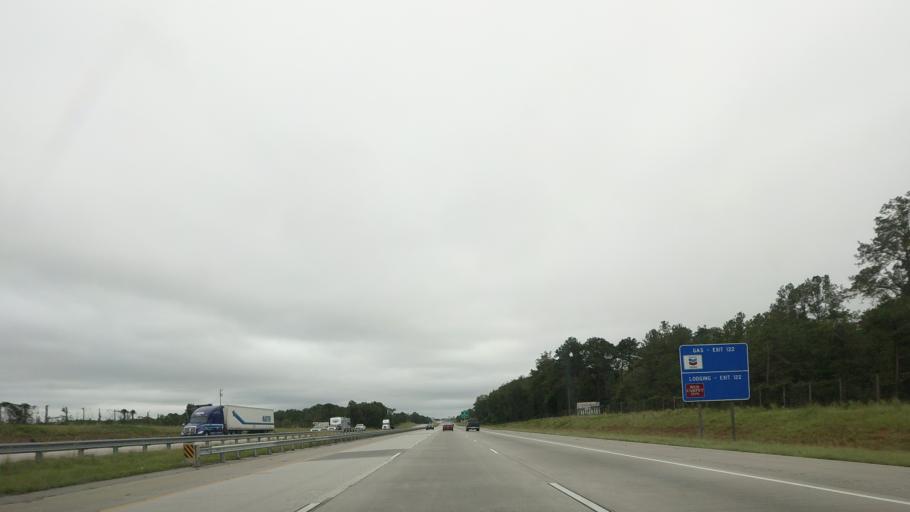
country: US
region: Georgia
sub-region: Dooly County
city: Unadilla
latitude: 32.2796
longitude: -83.7558
